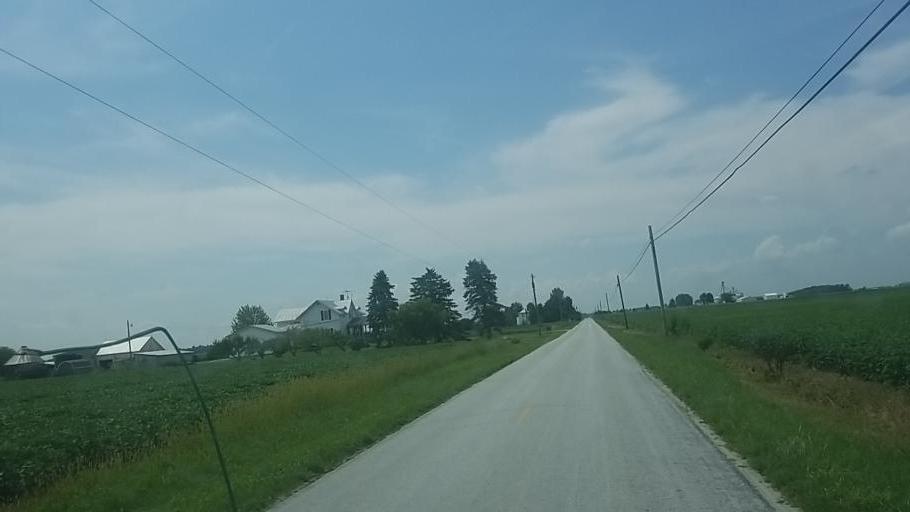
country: US
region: Ohio
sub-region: Hardin County
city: Kenton
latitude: 40.6574
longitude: -83.5018
